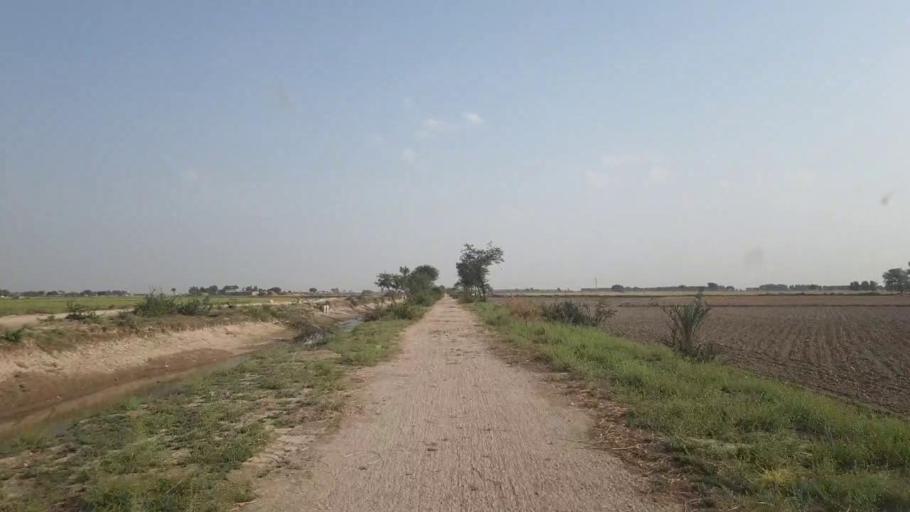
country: PK
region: Sindh
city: Kario
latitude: 24.5990
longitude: 68.5524
